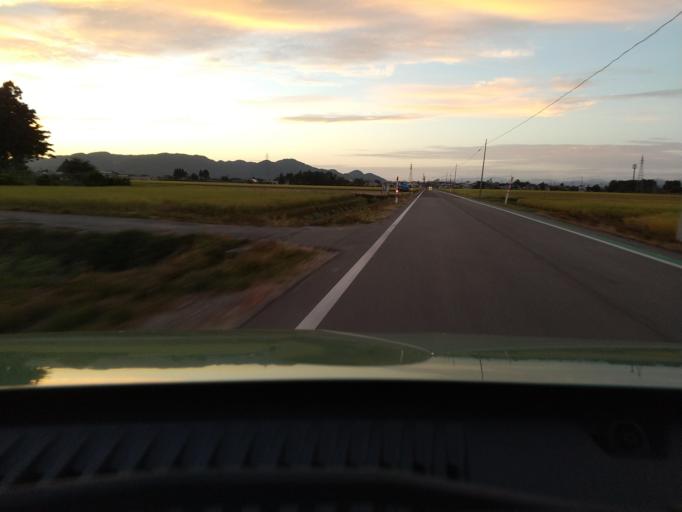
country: JP
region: Akita
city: Omagari
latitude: 39.4221
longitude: 140.4920
